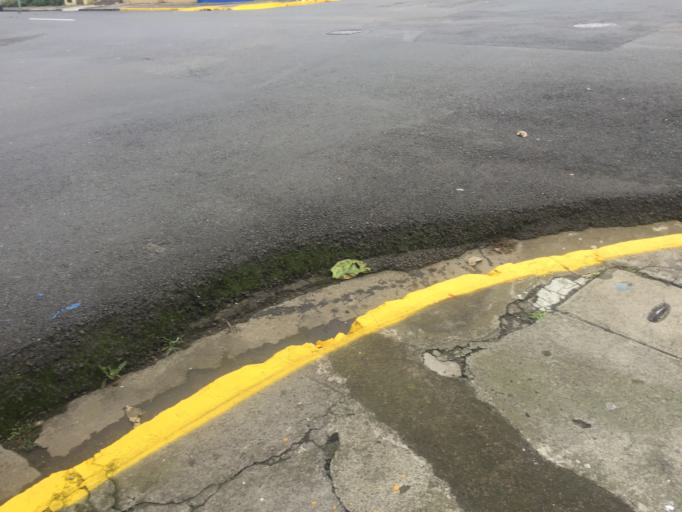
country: CR
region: Heredia
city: Heredia
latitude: 10.0040
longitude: -84.1192
